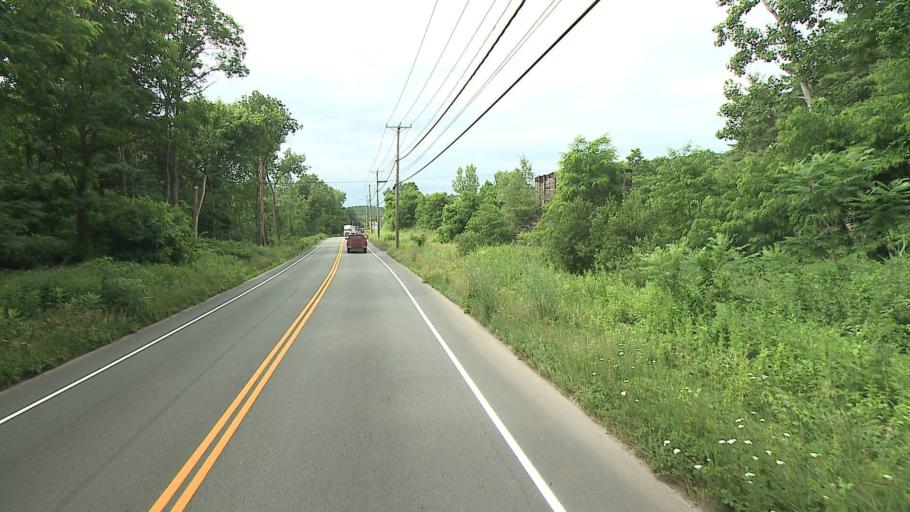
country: US
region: Connecticut
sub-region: Litchfield County
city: Torrington
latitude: 41.7817
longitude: -73.1176
